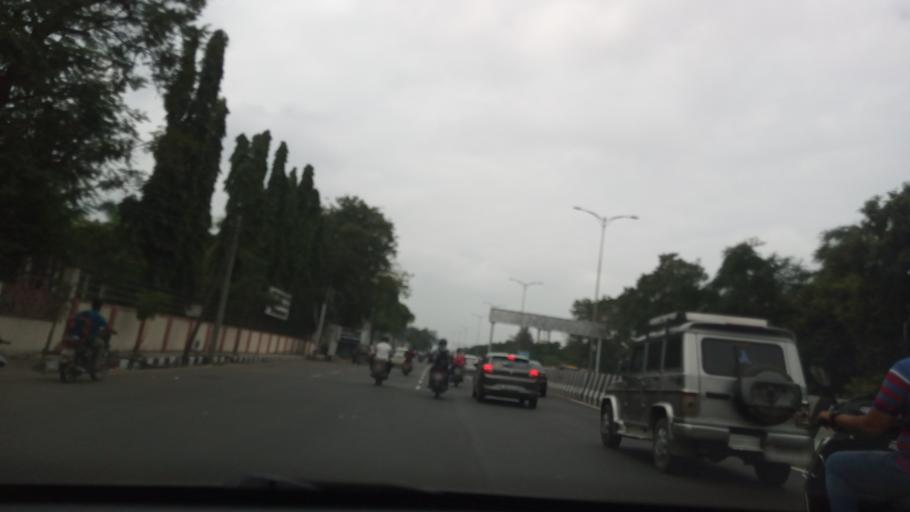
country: IN
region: Tamil Nadu
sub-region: Kancheepuram
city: Pallavaram
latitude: 12.9761
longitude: 80.1573
